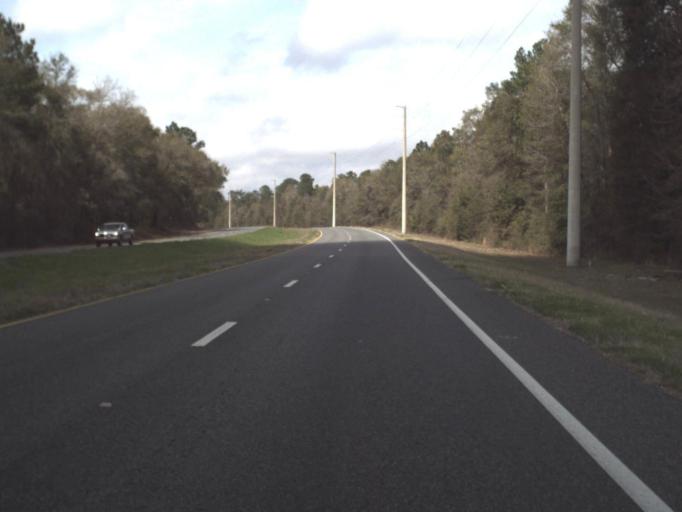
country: US
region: Florida
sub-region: Leon County
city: Woodville
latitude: 30.4176
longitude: -84.0895
